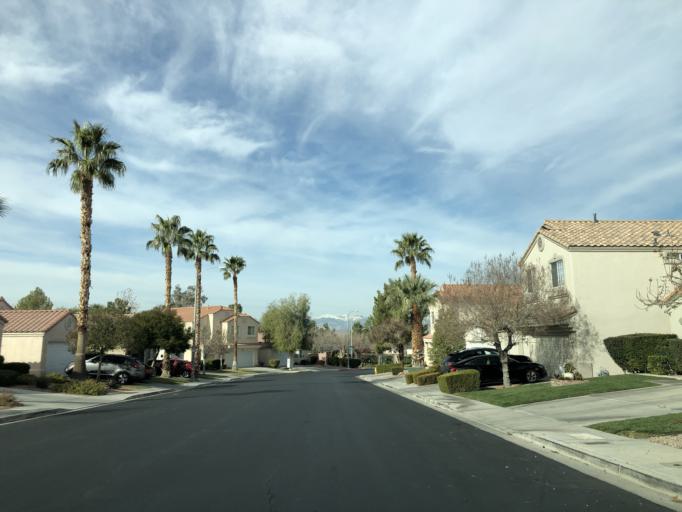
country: US
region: Nevada
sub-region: Clark County
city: Whitney
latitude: 36.0135
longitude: -115.0960
